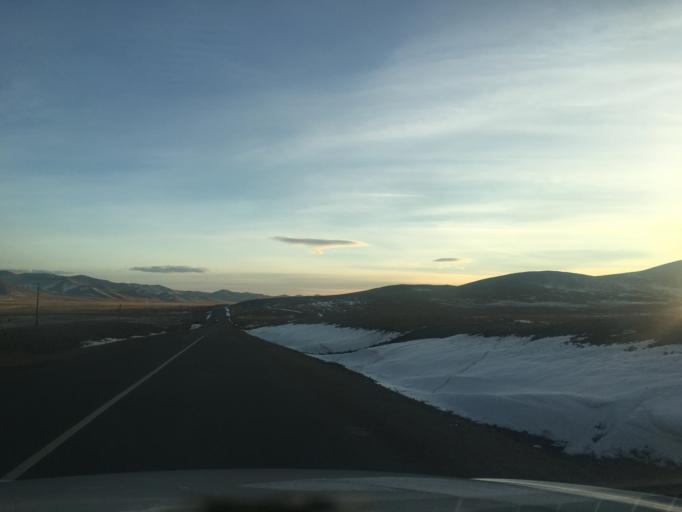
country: MN
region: Central Aimak
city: Mandal
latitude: 48.1866
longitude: 106.7048
